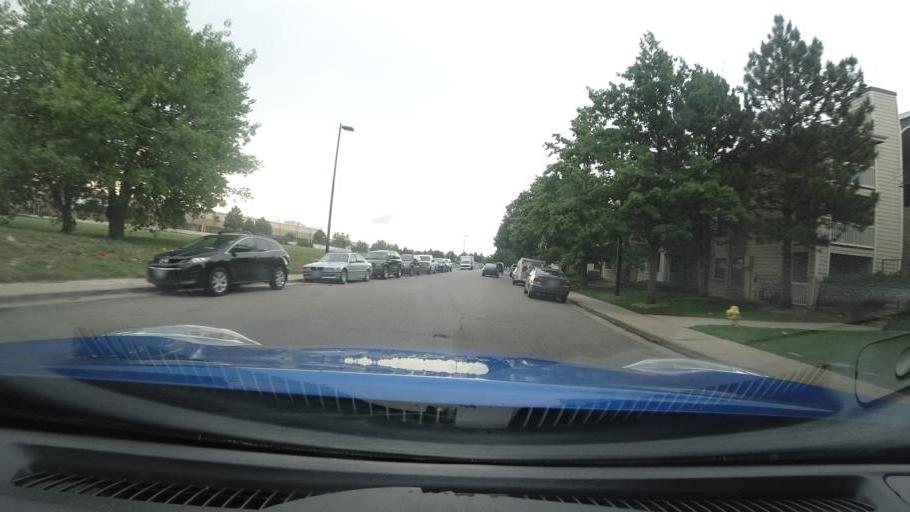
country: US
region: Colorado
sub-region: Adams County
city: Aurora
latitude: 39.6995
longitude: -104.8240
